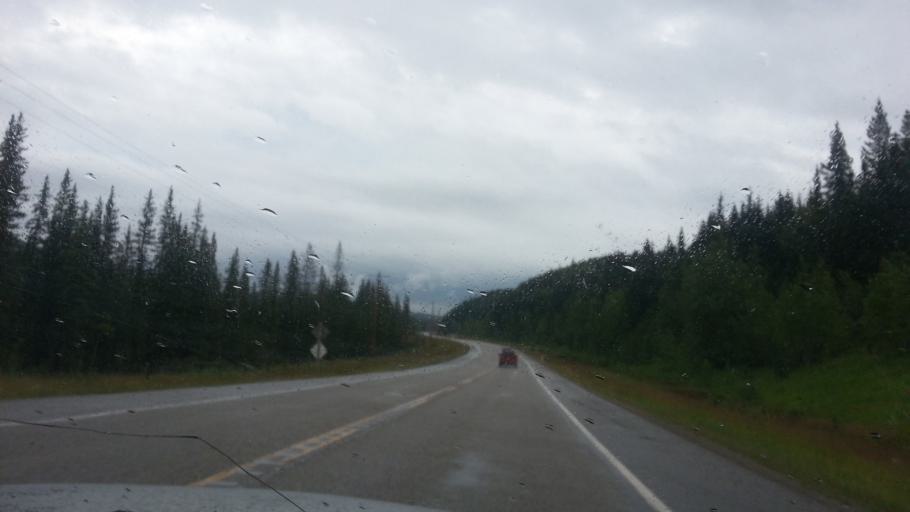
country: CA
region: Alberta
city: Cochrane
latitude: 50.9131
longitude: -114.6246
